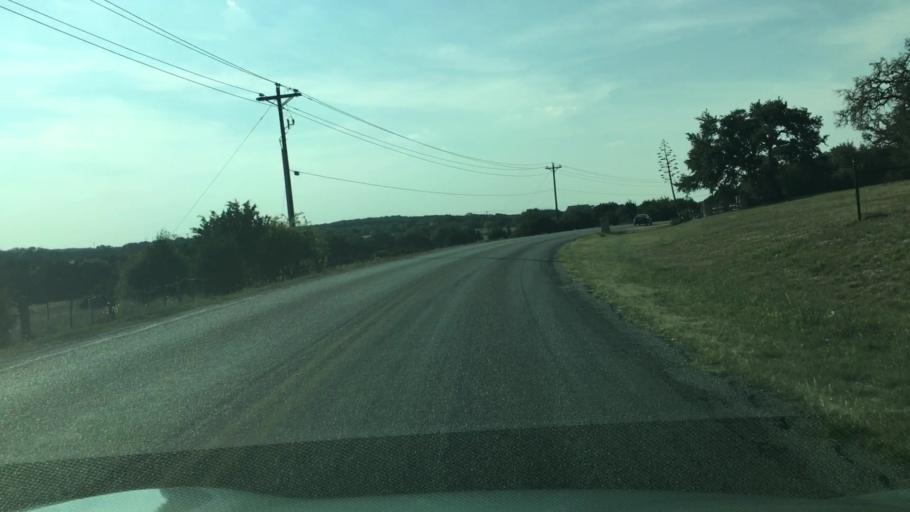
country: US
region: Texas
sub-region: Hays County
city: Dripping Springs
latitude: 30.1504
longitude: -97.9930
